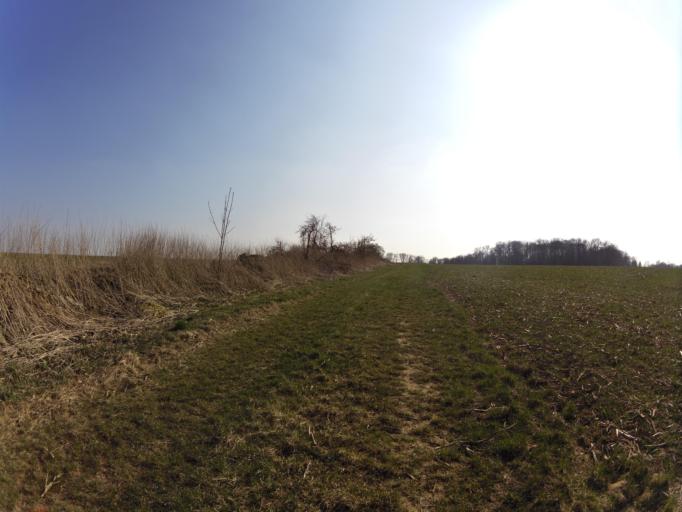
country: DE
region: Bavaria
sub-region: Regierungsbezirk Unterfranken
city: Gaukonigshofen
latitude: 49.6626
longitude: 9.9854
